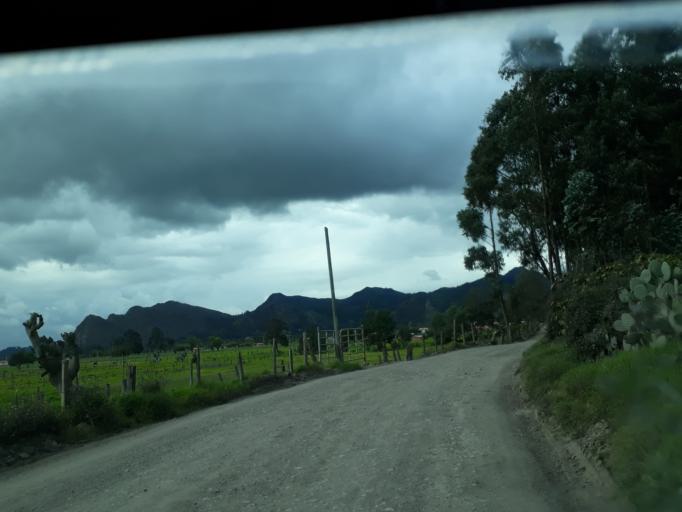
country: CO
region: Cundinamarca
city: Cucunuba
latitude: 5.2486
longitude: -73.7869
